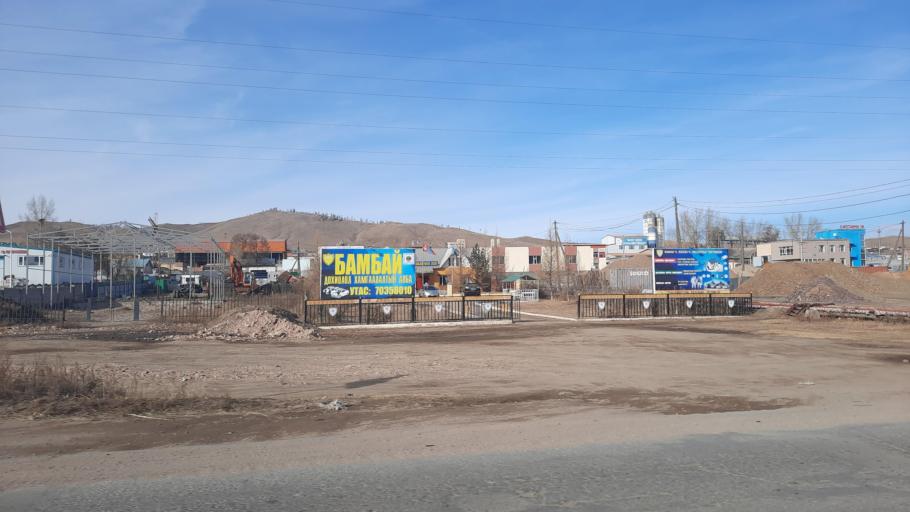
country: MN
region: Orhon
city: Erdenet
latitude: 49.0371
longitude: 104.0931
